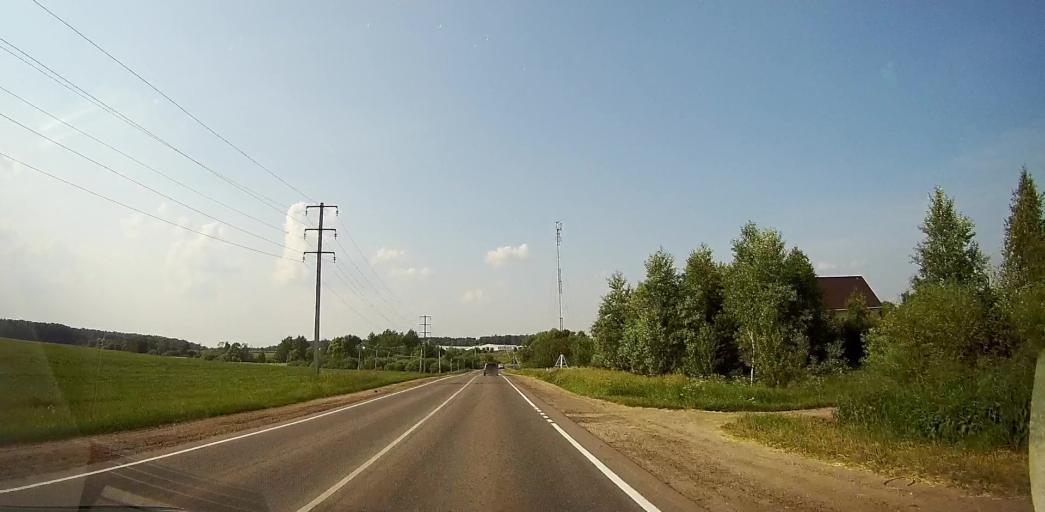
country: RU
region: Moskovskaya
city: Barybino
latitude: 55.2992
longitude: 37.9113
